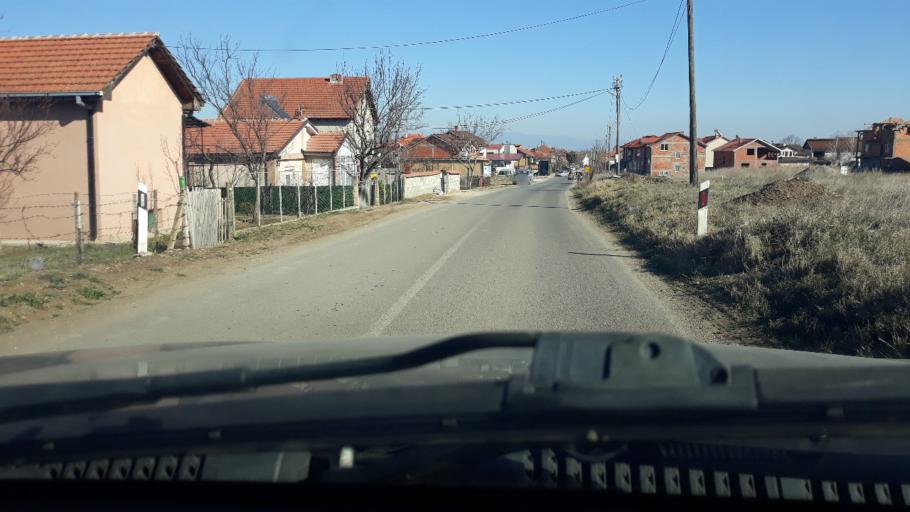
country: MK
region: Sveti Nikole
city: Sveti Nikole
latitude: 41.8701
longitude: 21.9292
